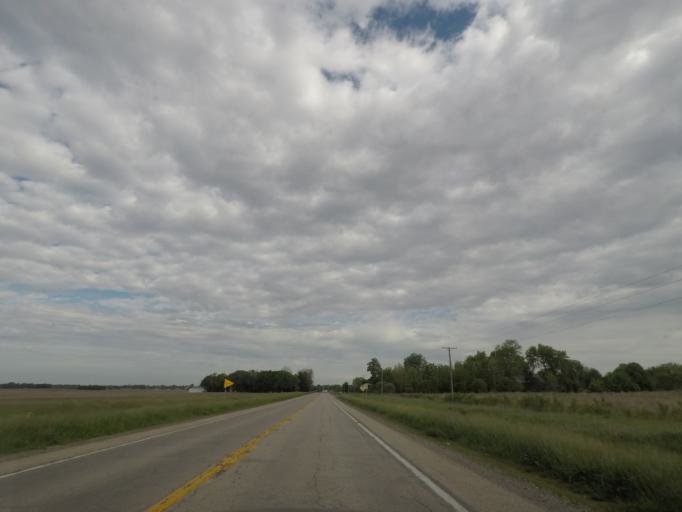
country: US
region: Illinois
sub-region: Logan County
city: Lincoln
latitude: 40.1257
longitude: -89.3402
